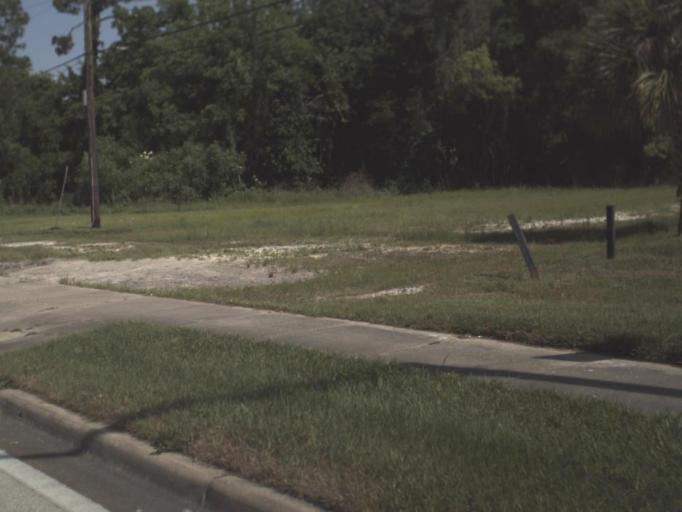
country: US
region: Florida
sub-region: Duval County
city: Jacksonville
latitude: 30.2914
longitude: -81.5979
